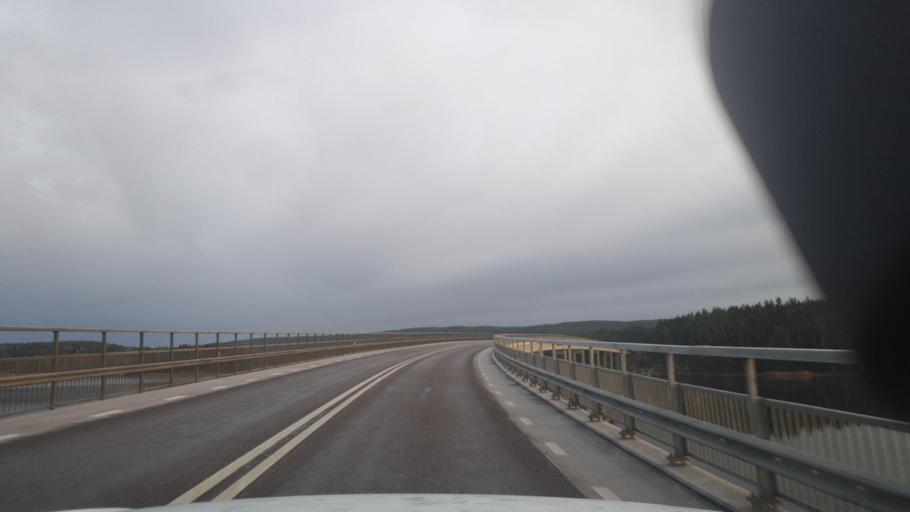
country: SE
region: Vaermland
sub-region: Arvika Kommun
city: Arvika
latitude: 59.4551
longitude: 12.7641
